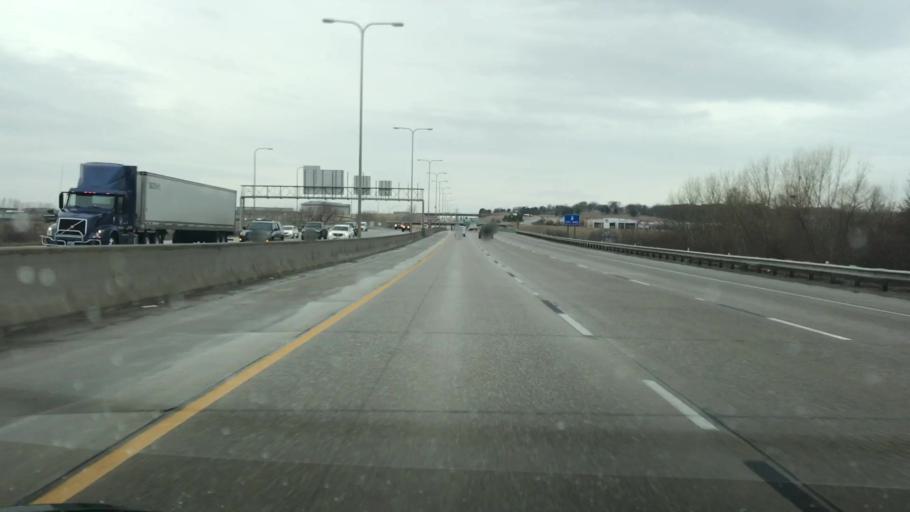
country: US
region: Nebraska
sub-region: Sarpy County
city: Chalco
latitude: 41.1918
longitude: -96.0996
